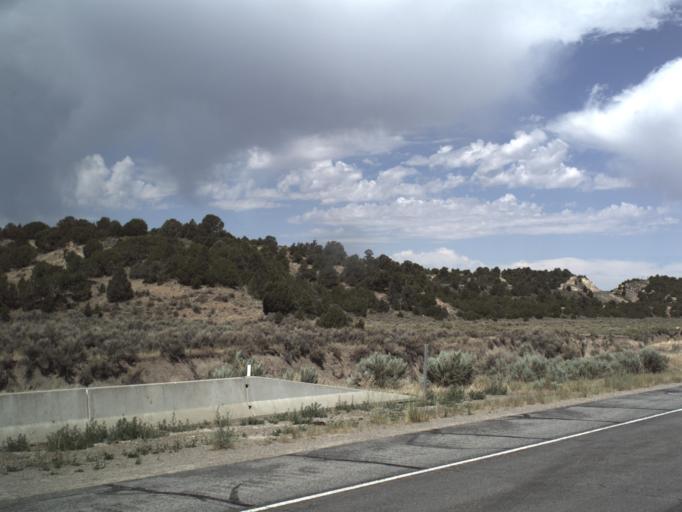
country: US
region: Utah
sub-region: Utah County
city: Eagle Mountain
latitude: 39.9863
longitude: -112.2642
